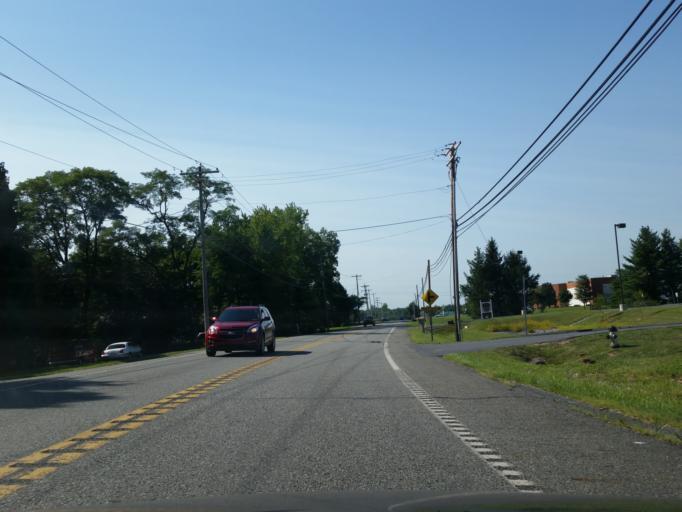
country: US
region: Pennsylvania
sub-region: Lebanon County
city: Jonestown
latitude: 40.4615
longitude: -76.5128
